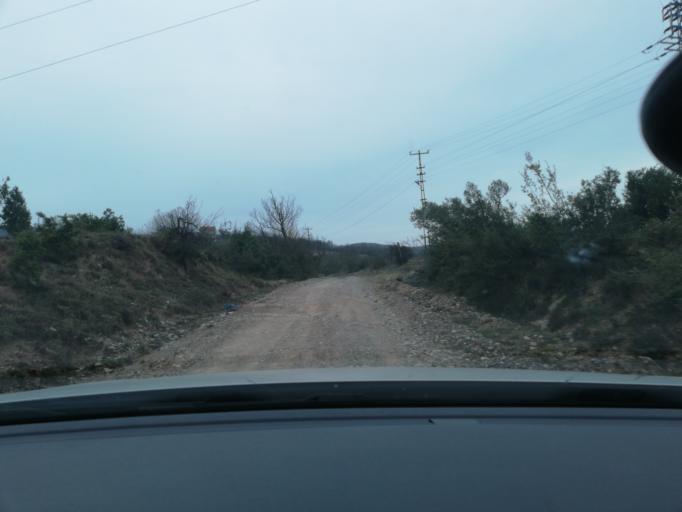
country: TR
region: Zonguldak
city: Saltukova
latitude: 41.5175
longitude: 32.0743
